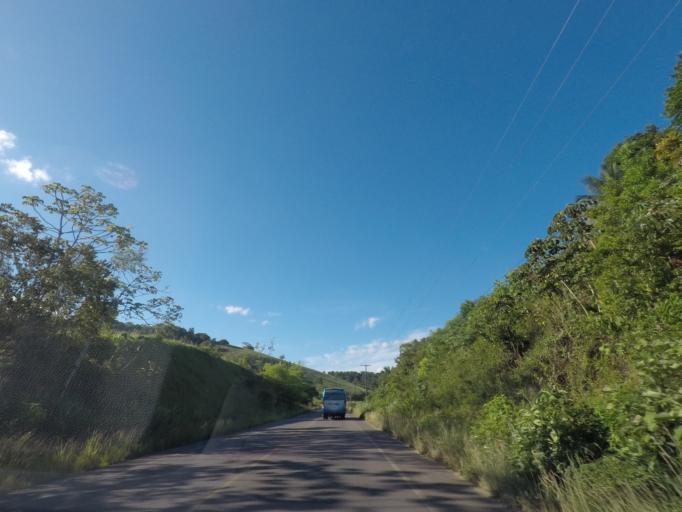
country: BR
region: Bahia
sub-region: Nazare
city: Nazare
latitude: -13.0528
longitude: -39.0056
